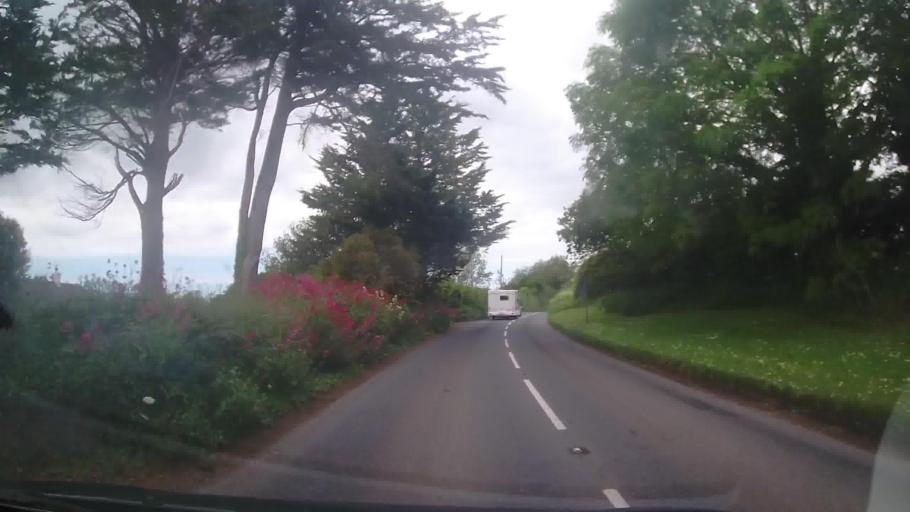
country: GB
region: England
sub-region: Devon
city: Kingsbridge
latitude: 50.2694
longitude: -3.7567
